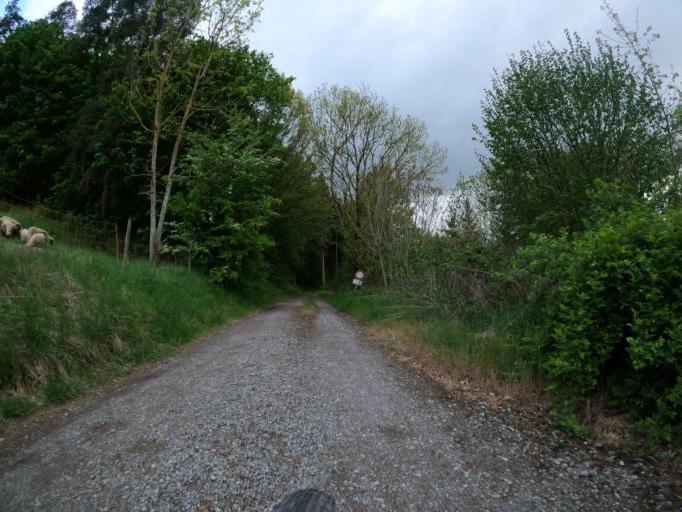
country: DE
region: Baden-Wuerttemberg
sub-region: Regierungsbezirk Stuttgart
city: Aidlingen
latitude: 48.6977
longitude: 8.9265
